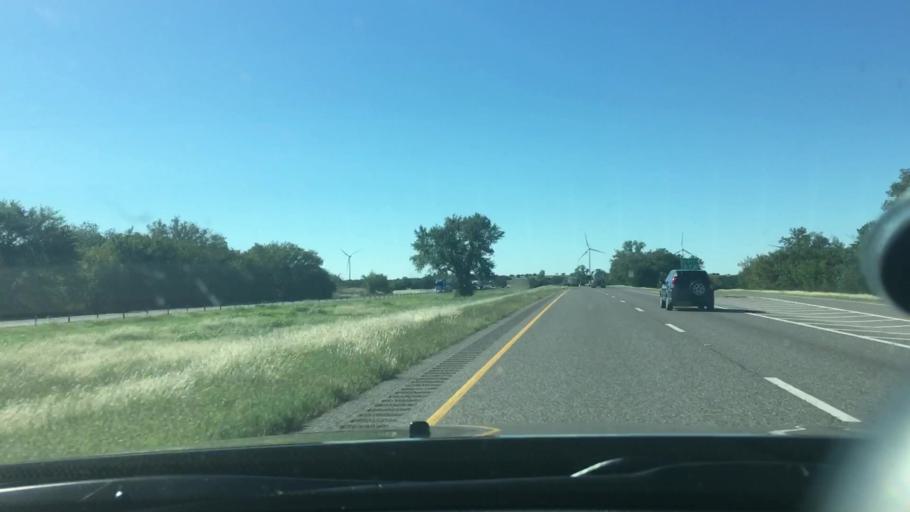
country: US
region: Oklahoma
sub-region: Murray County
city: Davis
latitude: 34.4042
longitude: -97.1406
